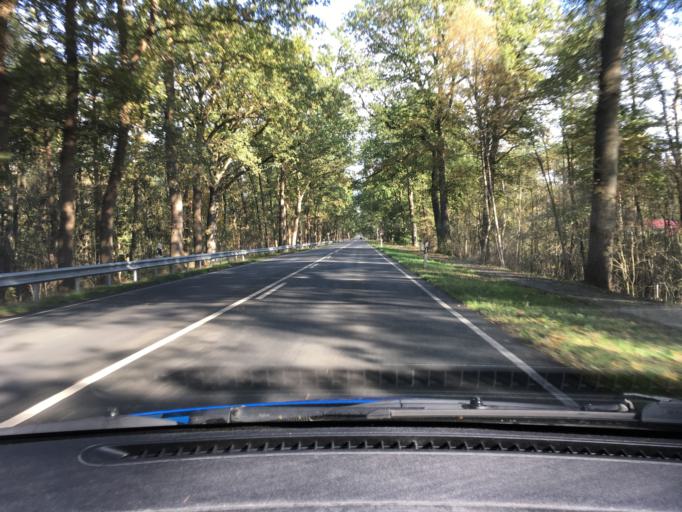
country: DE
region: Lower Saxony
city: Wistedt
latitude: 53.2563
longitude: 9.6459
